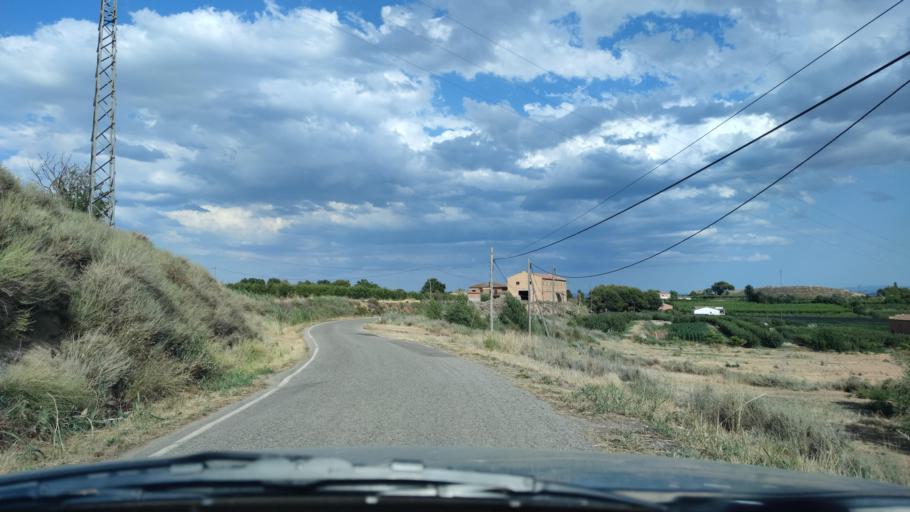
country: ES
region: Catalonia
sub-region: Provincia de Lleida
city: Alpicat
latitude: 41.6299
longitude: 0.5666
